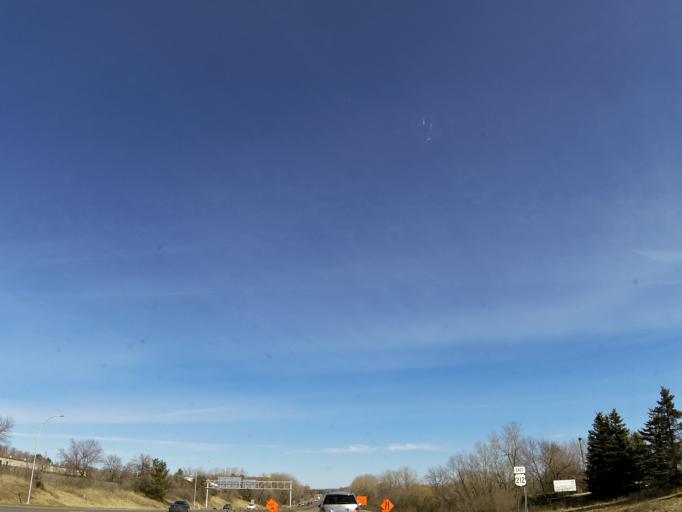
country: US
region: Minnesota
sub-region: Hennepin County
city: Eden Prairie
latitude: 44.8702
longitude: -93.4160
